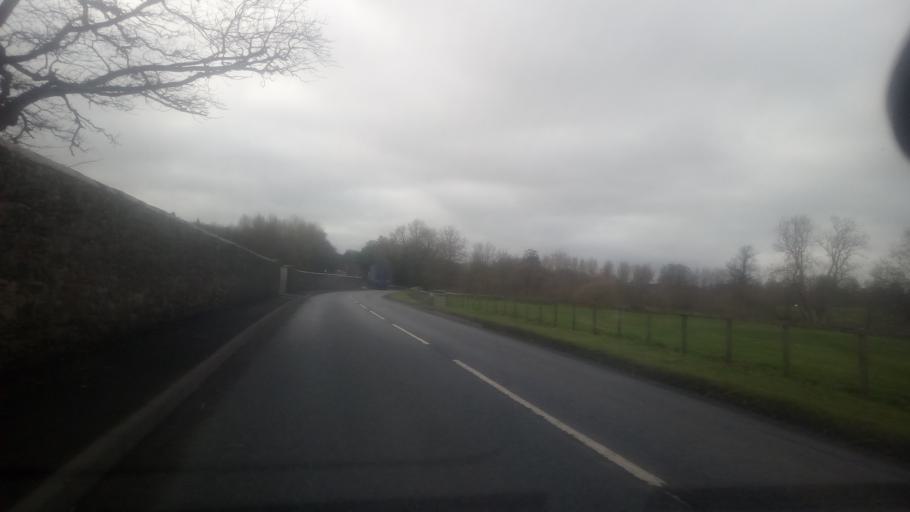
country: GB
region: Scotland
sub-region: The Scottish Borders
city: Kelso
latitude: 55.5966
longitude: -2.4410
